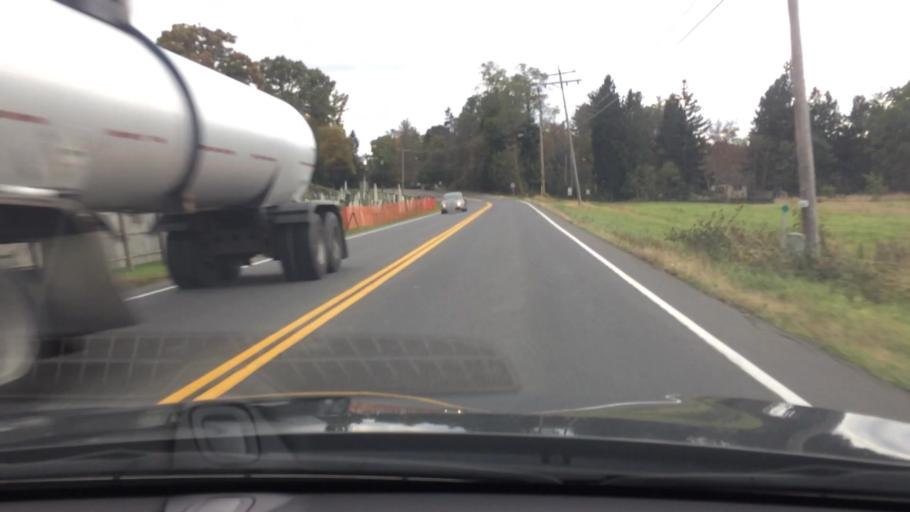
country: US
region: New York
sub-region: Columbia County
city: Lorenz Park
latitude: 42.2299
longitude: -73.7338
